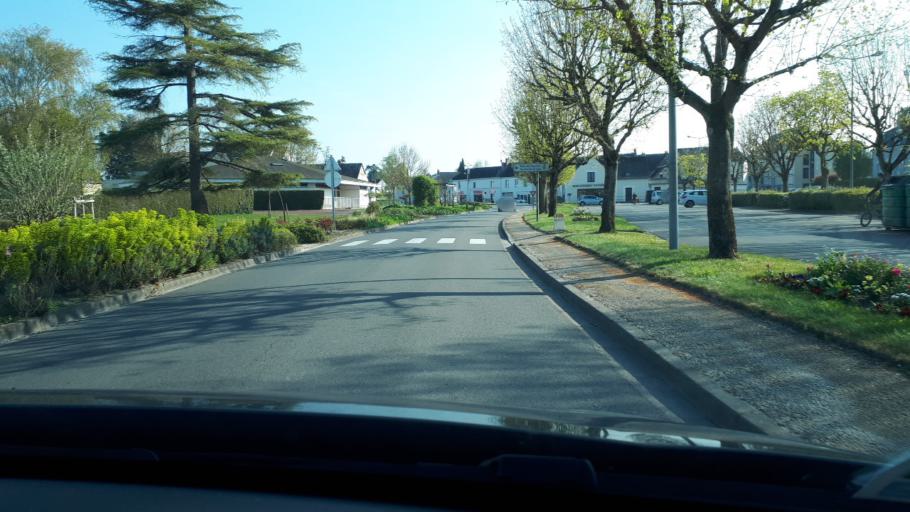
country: FR
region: Centre
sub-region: Departement d'Indre-et-Loire
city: Blere
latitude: 47.3275
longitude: 0.9953
